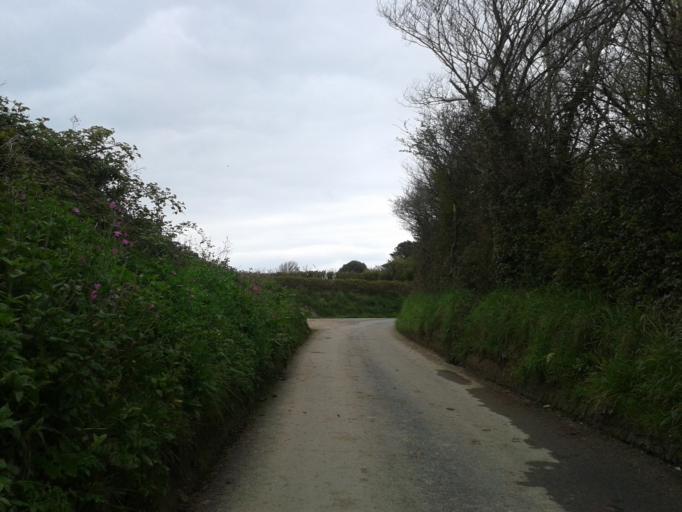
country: GB
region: England
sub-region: Devon
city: Braunton
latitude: 51.1384
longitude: -4.2209
